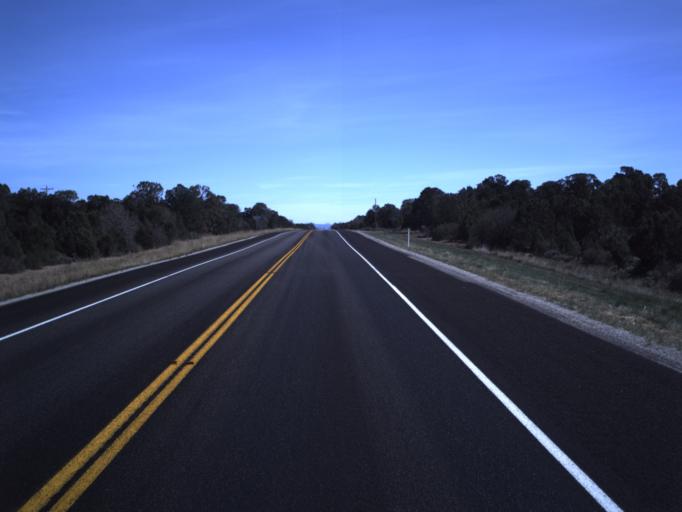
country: US
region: Utah
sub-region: San Juan County
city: Monticello
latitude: 37.8603
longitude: -109.2087
